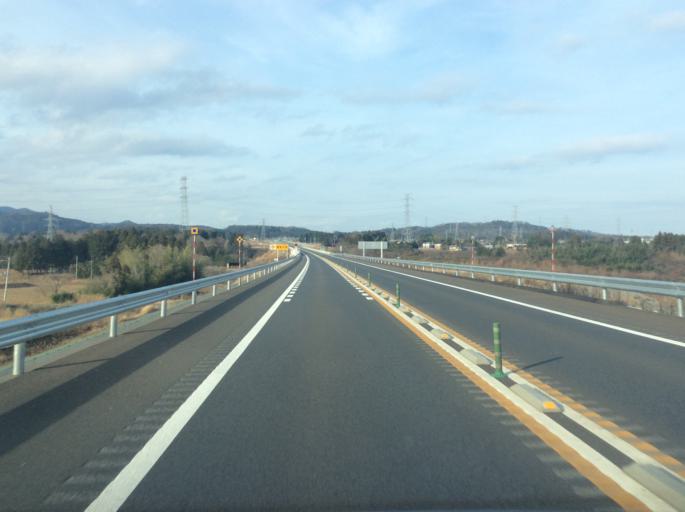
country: JP
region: Fukushima
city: Namie
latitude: 37.3941
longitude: 140.9661
